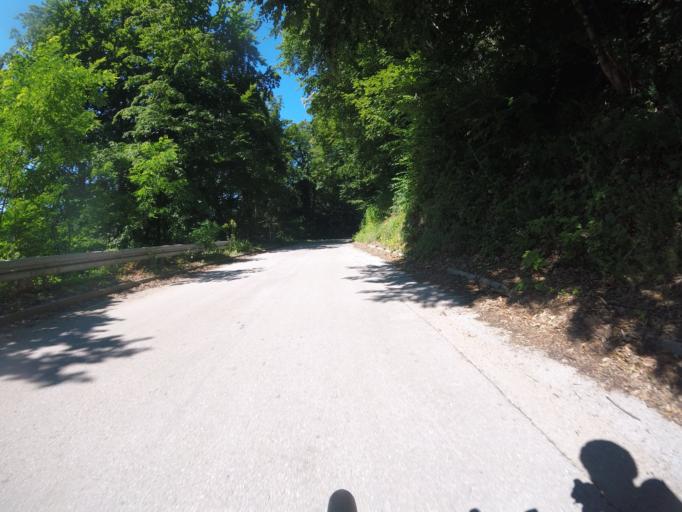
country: SI
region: Brezice
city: Brezice
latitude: 45.8257
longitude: 15.5531
